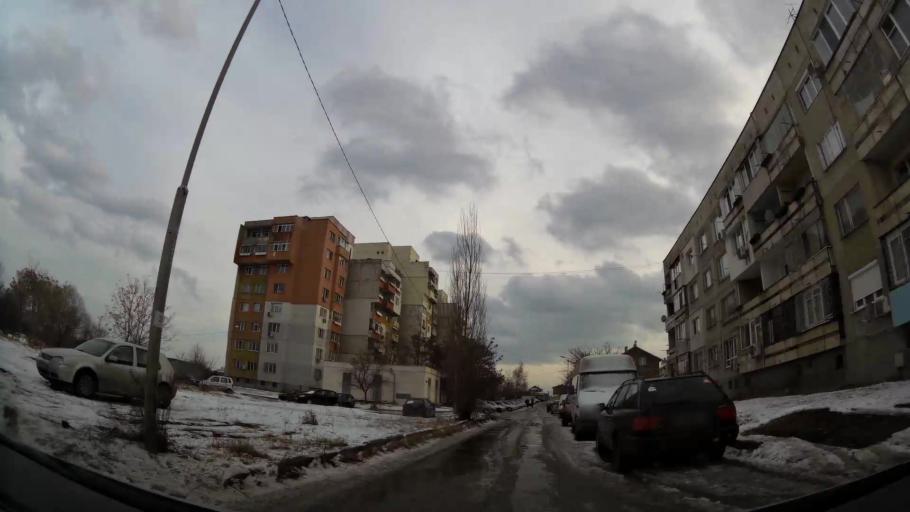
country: BG
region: Sofia-Capital
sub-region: Stolichna Obshtina
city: Sofia
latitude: 42.7284
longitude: 23.3453
